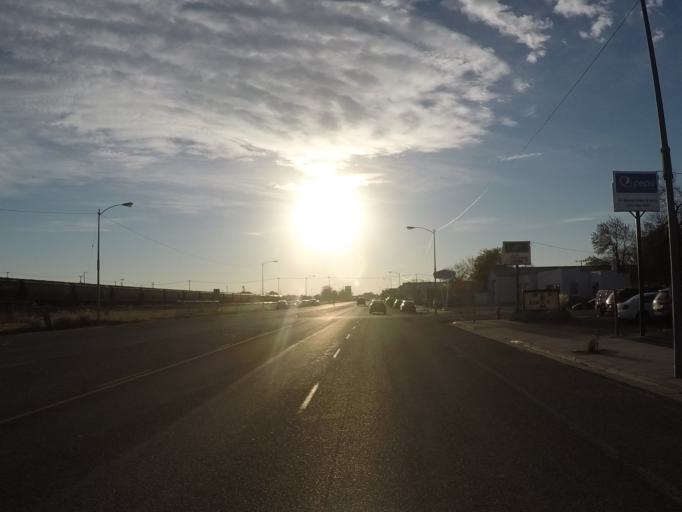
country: US
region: Montana
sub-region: Yellowstone County
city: Laurel
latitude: 45.6715
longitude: -108.7624
